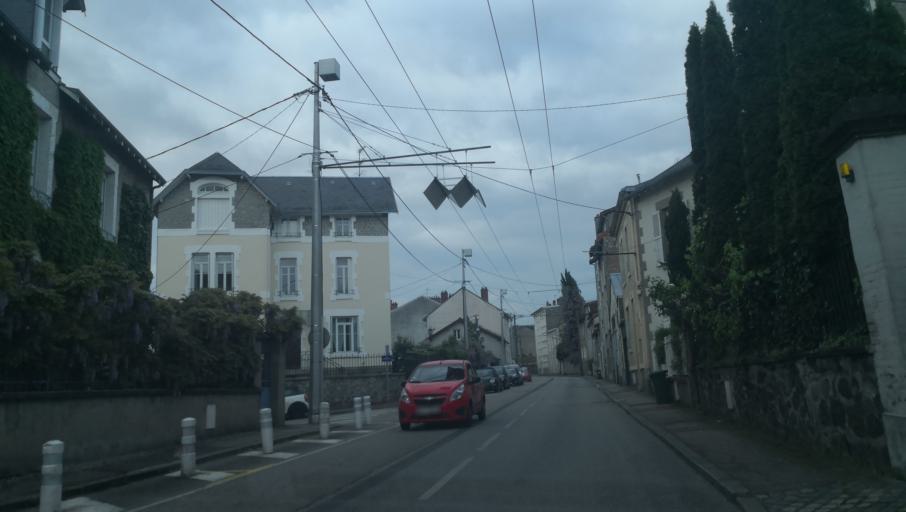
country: FR
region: Limousin
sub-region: Departement de la Haute-Vienne
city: Limoges
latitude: 45.8329
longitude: 1.2444
